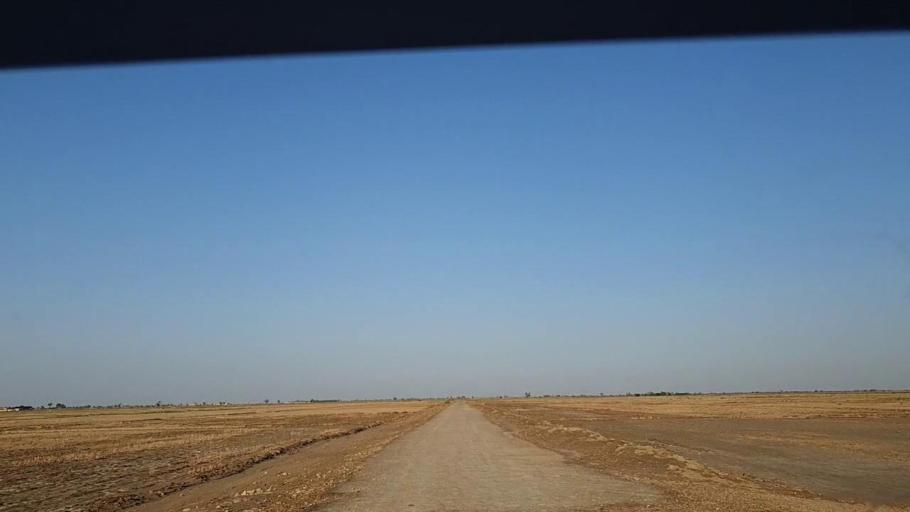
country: PK
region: Sindh
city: Johi
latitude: 26.7444
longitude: 67.6203
